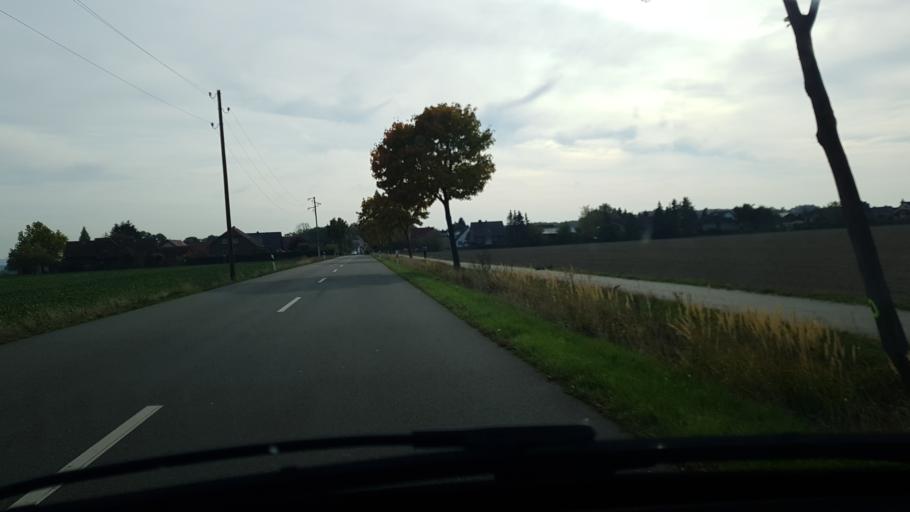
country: DE
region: Lower Saxony
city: Lehre
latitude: 52.3570
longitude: 10.6712
